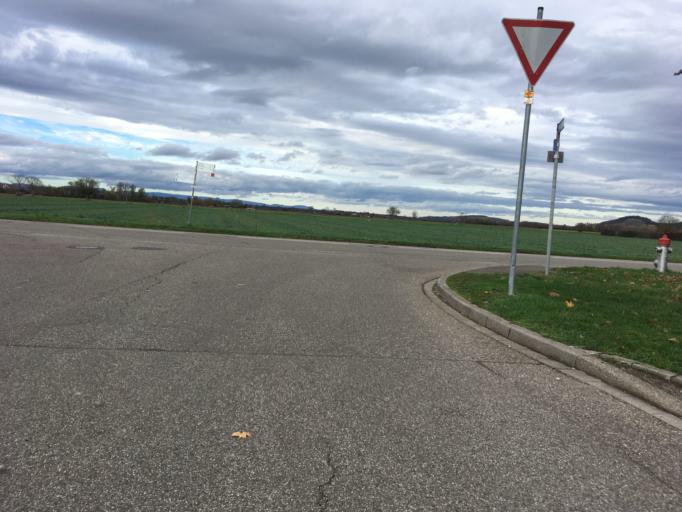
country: DE
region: Baden-Wuerttemberg
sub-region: Freiburg Region
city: Breisach am Rhein
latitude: 48.0342
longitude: 7.5978
